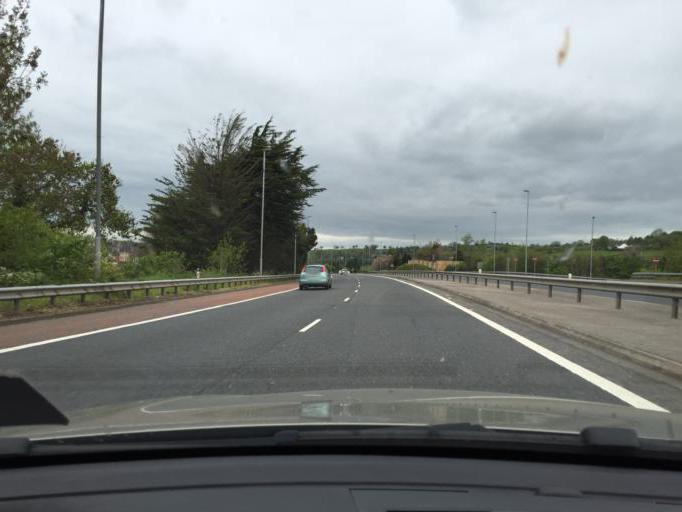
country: GB
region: Northern Ireland
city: Hillsborough
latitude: 54.4206
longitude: -6.1346
